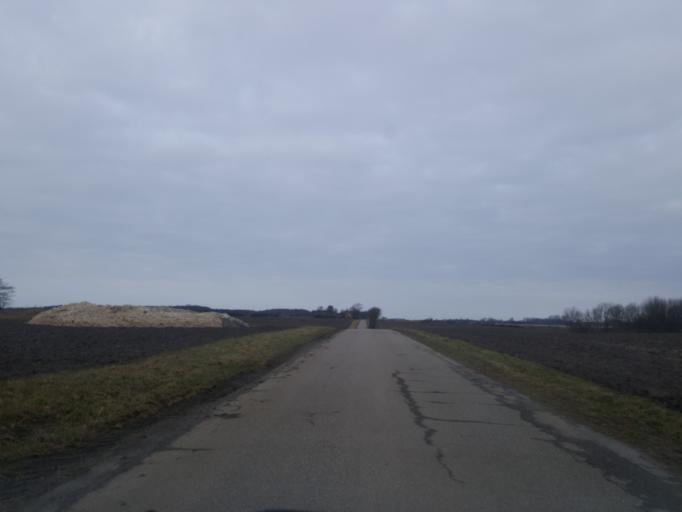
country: DK
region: Zealand
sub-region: Vordingborg Kommune
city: Neder Vindinge
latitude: 55.0243
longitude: 11.8627
